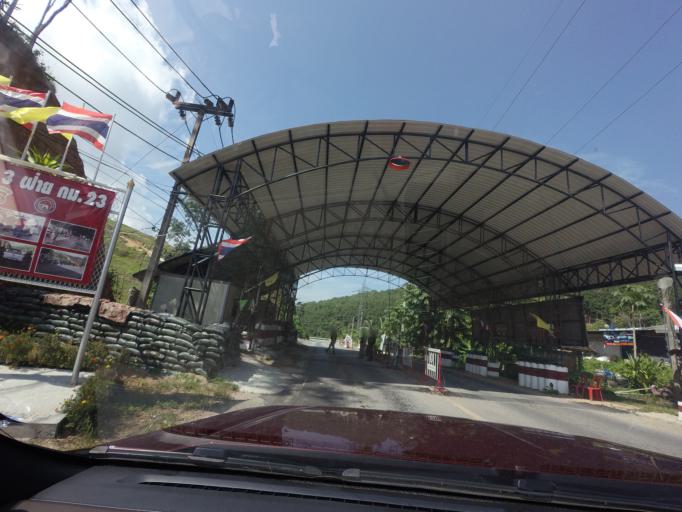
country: TH
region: Yala
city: Betong
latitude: 5.9015
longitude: 101.1452
